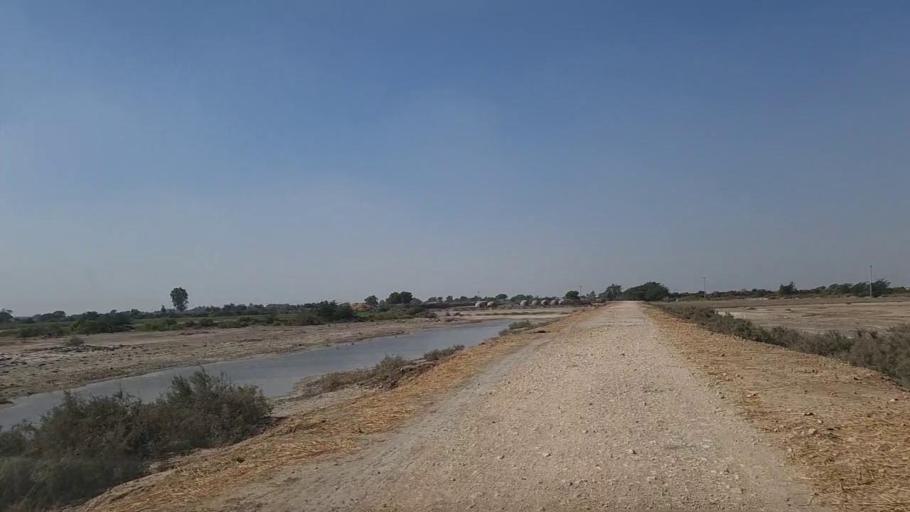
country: PK
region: Sindh
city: Daro Mehar
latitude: 24.8335
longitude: 68.1862
